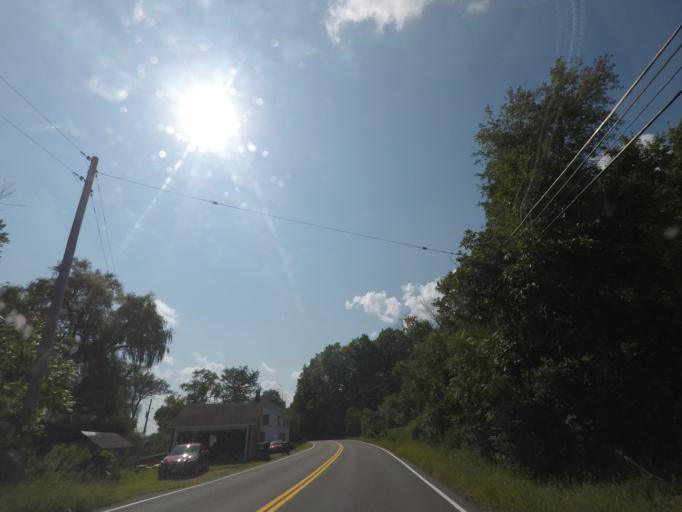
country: US
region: New York
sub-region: Rensselaer County
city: Poestenkill
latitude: 42.7699
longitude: -73.5504
